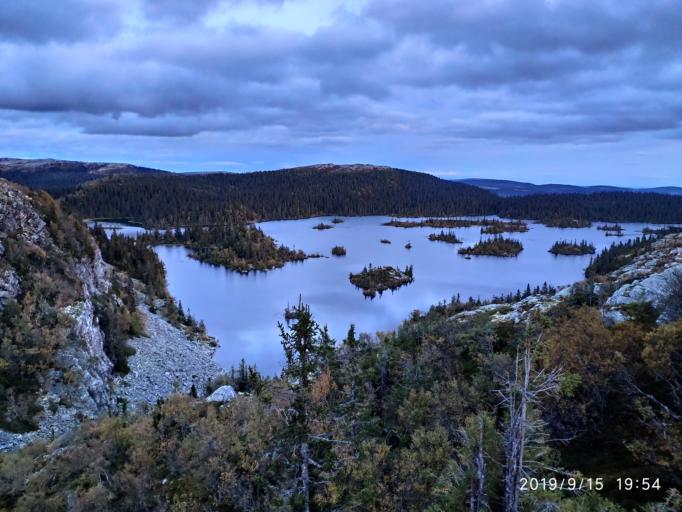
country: NO
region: Oppland
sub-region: Oyer
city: Tretten
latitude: 61.4245
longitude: 10.2622
